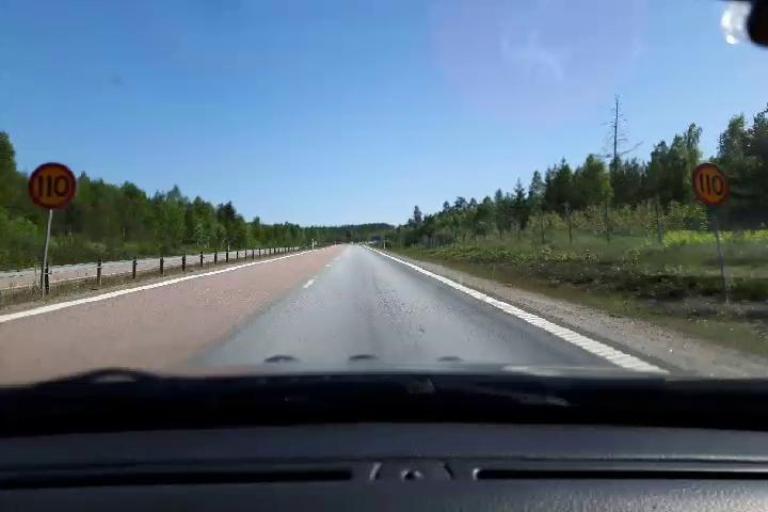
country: SE
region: Gaevleborg
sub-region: Hudiksvalls Kommun
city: Iggesund
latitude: 61.5186
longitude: 16.9789
